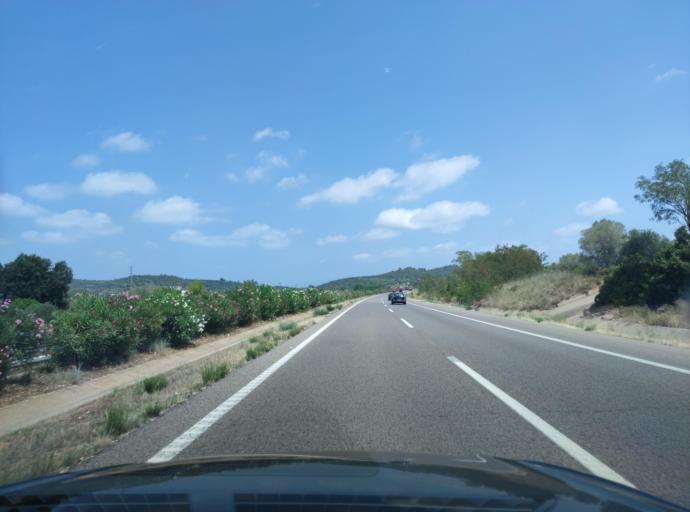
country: ES
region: Catalonia
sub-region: Provincia de Tarragona
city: Santa Barbara
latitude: 40.6581
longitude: 0.5101
